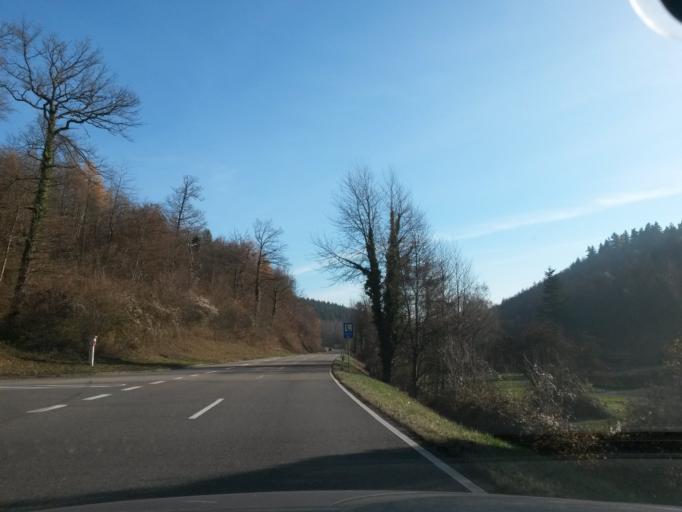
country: DE
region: Baden-Wuerttemberg
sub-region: Karlsruhe Region
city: Ispringen
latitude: 48.9290
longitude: 8.6487
